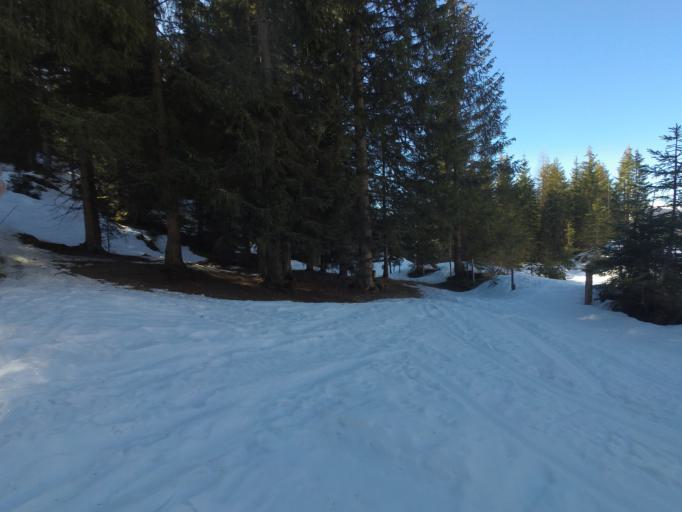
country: AT
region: Salzburg
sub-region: Politischer Bezirk Sankt Johann im Pongau
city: Muhlbach am Hochkonig
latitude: 47.3986
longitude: 13.1166
